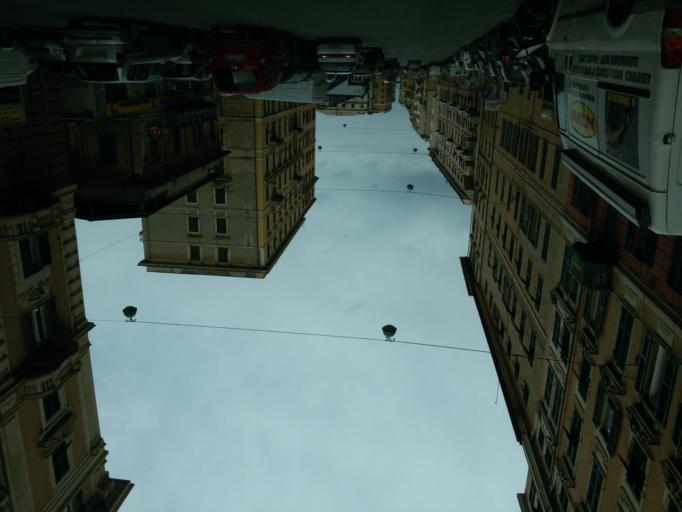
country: IT
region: Liguria
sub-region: Provincia di Genova
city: San Teodoro
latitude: 44.4106
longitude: 8.8871
